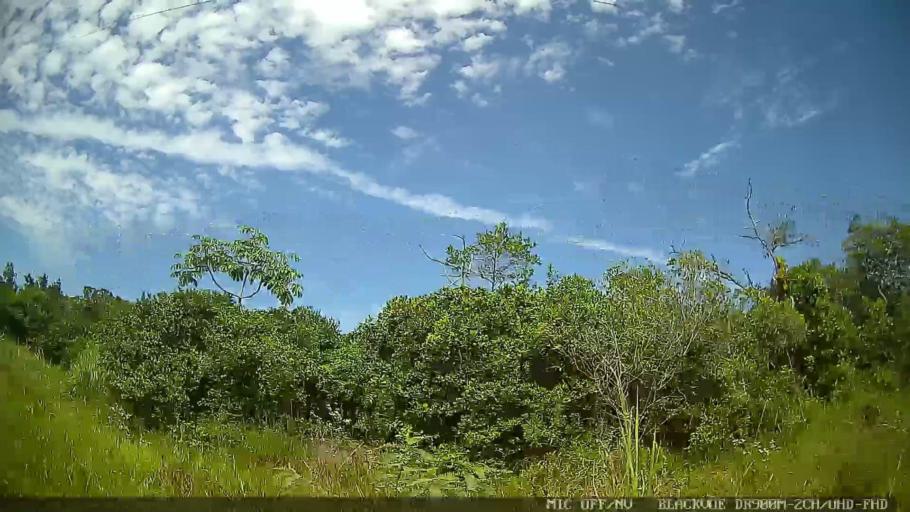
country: BR
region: Sao Paulo
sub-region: Iguape
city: Iguape
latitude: -24.7159
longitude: -47.5200
